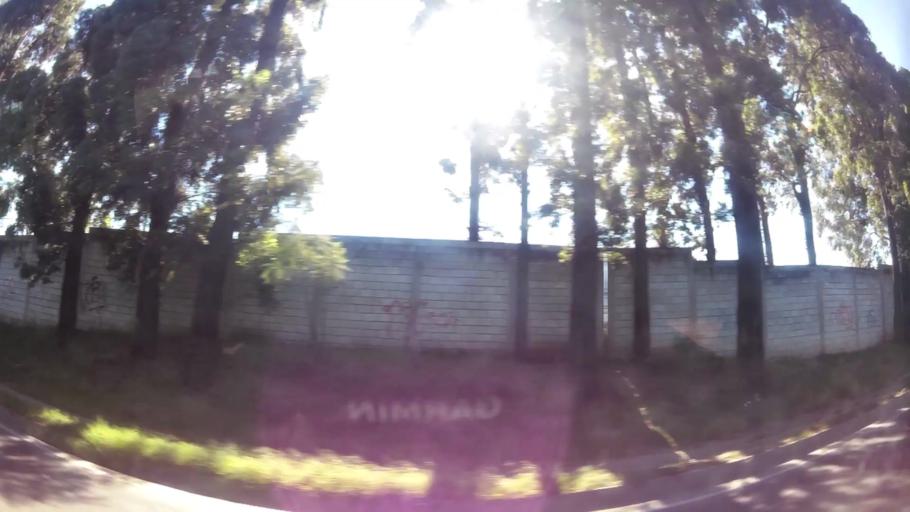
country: GT
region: Guatemala
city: Villa Nueva
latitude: 14.5387
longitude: -90.6074
